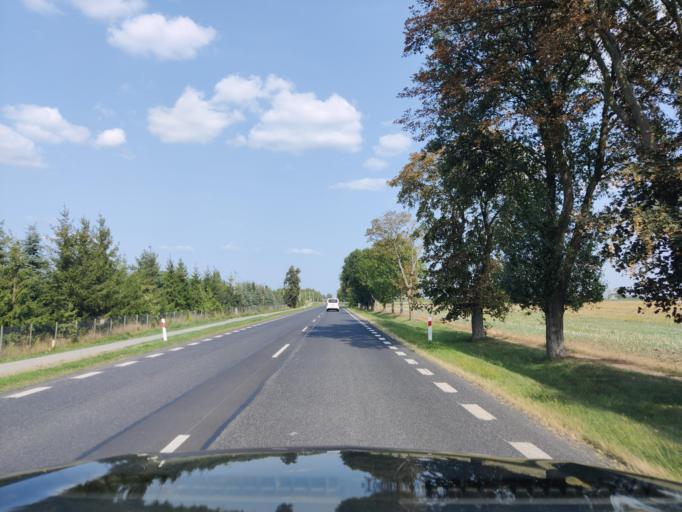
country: PL
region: Masovian Voivodeship
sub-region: Powiat makowski
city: Rozan
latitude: 52.8808
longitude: 21.3724
